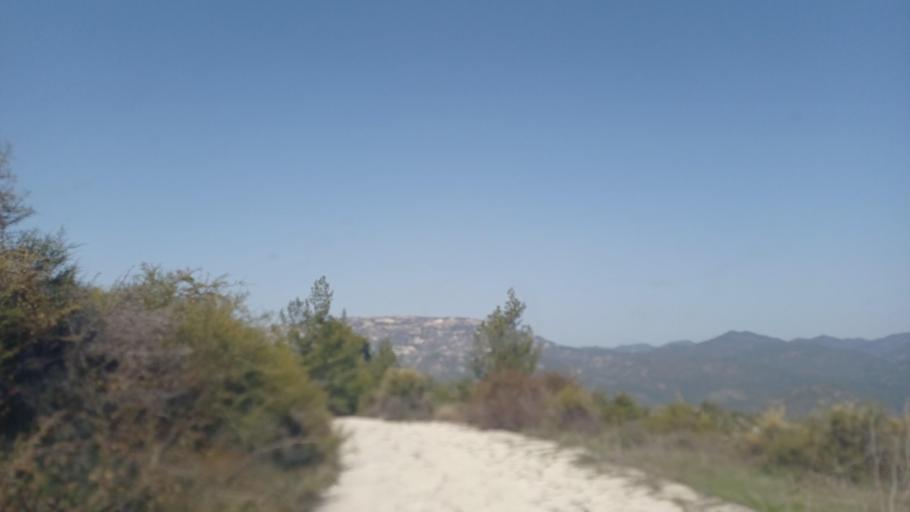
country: CY
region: Limassol
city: Pachna
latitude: 34.8787
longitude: 32.7075
